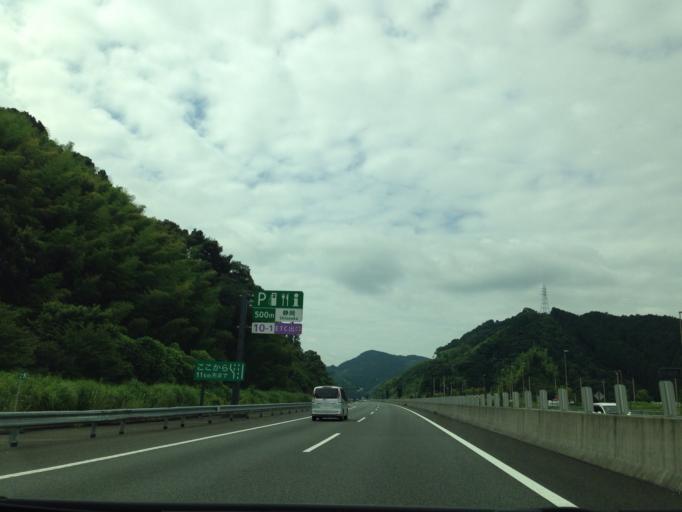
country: JP
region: Shizuoka
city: Shizuoka-shi
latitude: 34.9831
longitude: 138.2954
